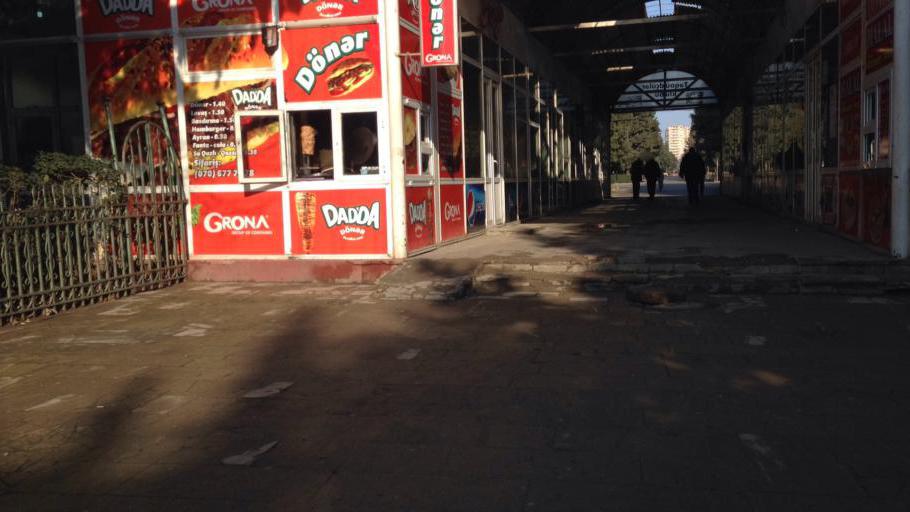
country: AZ
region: Baki
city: Baku
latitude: 40.4053
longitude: 49.8494
